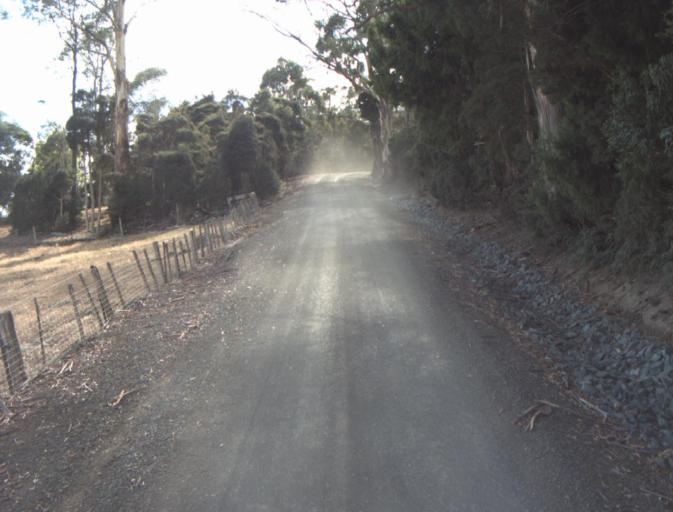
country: AU
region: Tasmania
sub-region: Launceston
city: Mayfield
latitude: -41.2628
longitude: 147.2289
